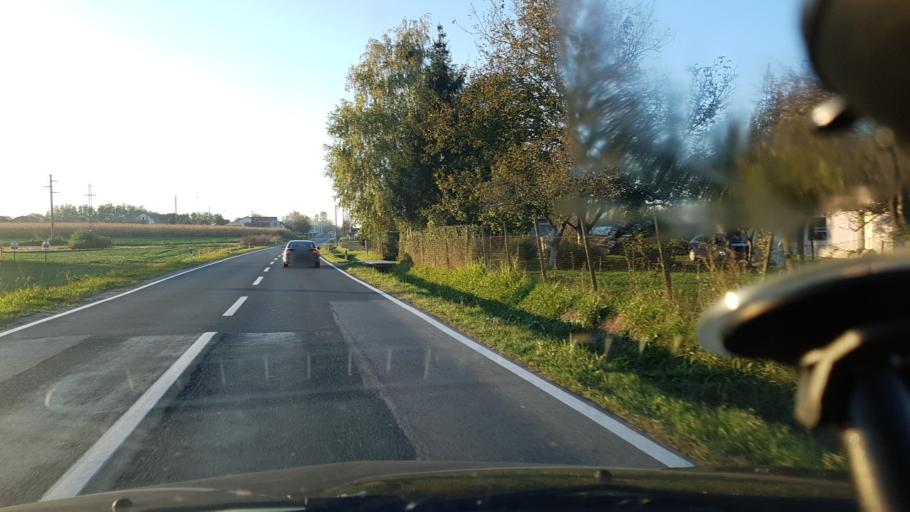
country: HR
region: Koprivnicko-Krizevacka
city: Peteranec
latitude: 46.1118
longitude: 16.8937
